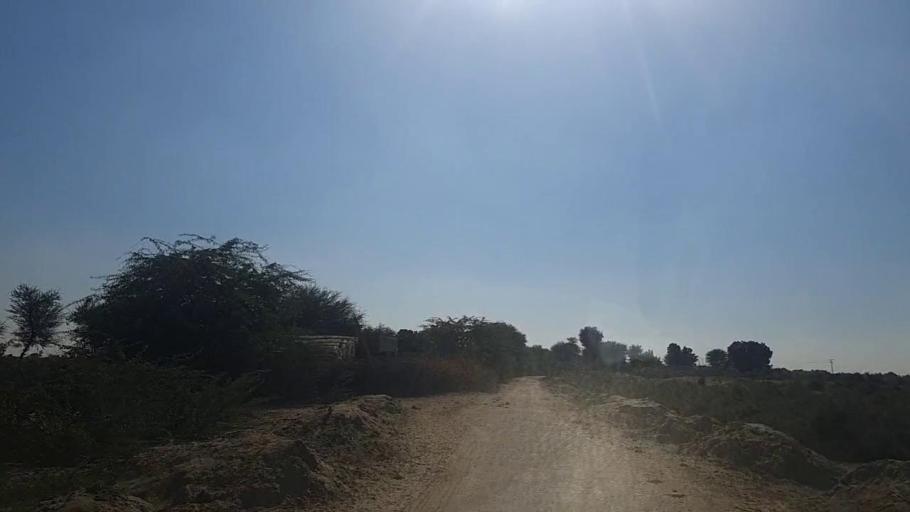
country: PK
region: Sindh
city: Khadro
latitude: 26.1563
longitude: 68.8380
